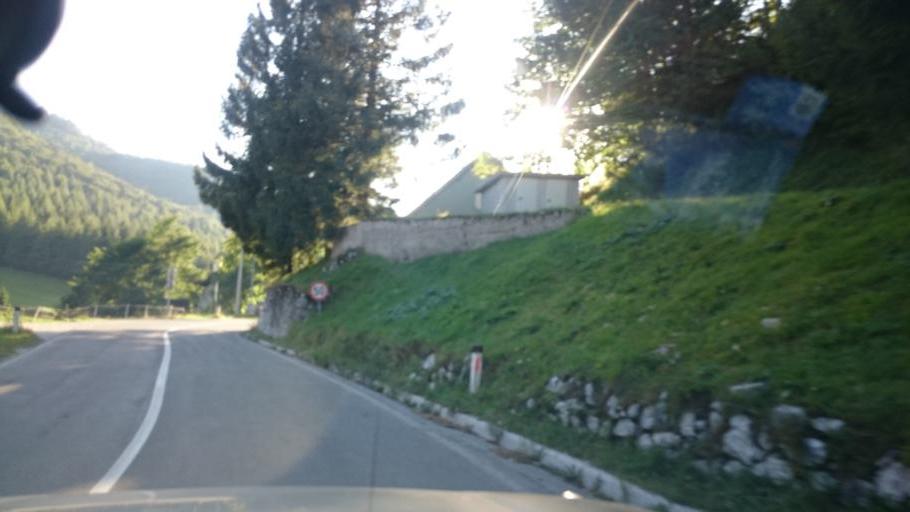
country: SI
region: Bovec
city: Bovec
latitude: 46.4191
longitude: 13.5803
